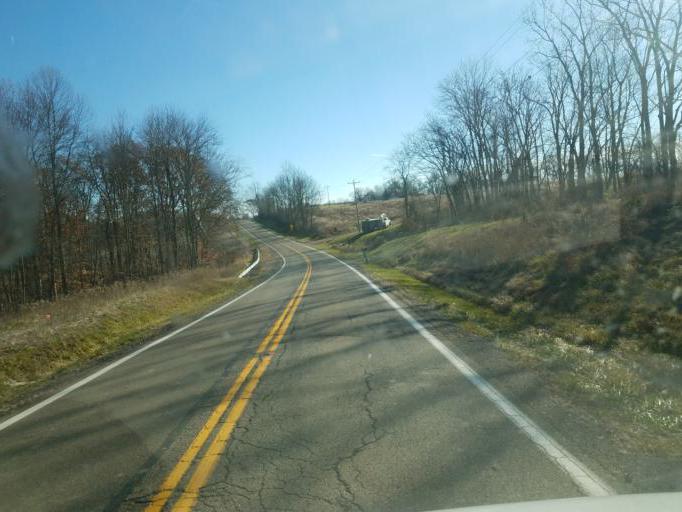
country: US
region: Ohio
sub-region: Muskingum County
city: Frazeysburg
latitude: 40.2819
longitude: -82.1396
